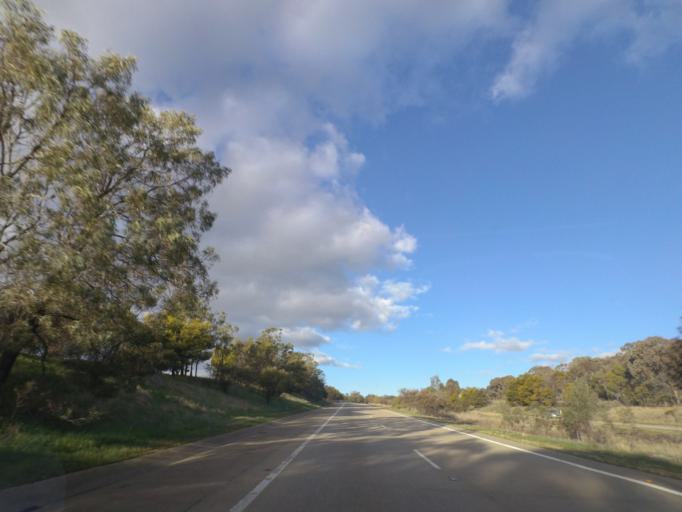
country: AU
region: New South Wales
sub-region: Yass Valley
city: Yass
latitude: -34.8030
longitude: 148.5525
